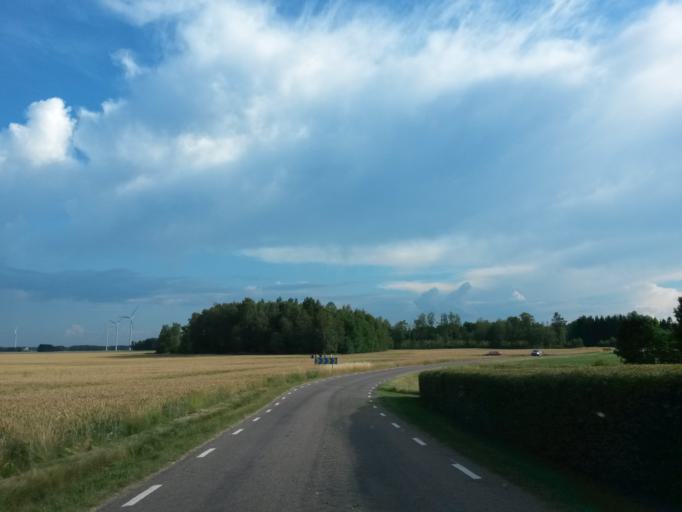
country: SE
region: Vaestra Goetaland
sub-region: Grastorps Kommun
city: Graestorp
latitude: 58.3519
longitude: 12.7794
